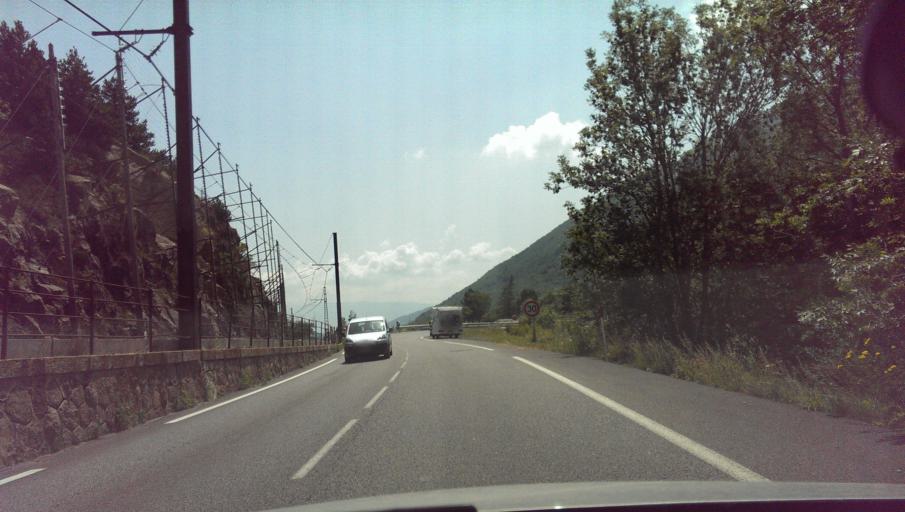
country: ES
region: Catalonia
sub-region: Provincia de Girona
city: Guils de Cerdanya
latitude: 42.5040
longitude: 1.8353
